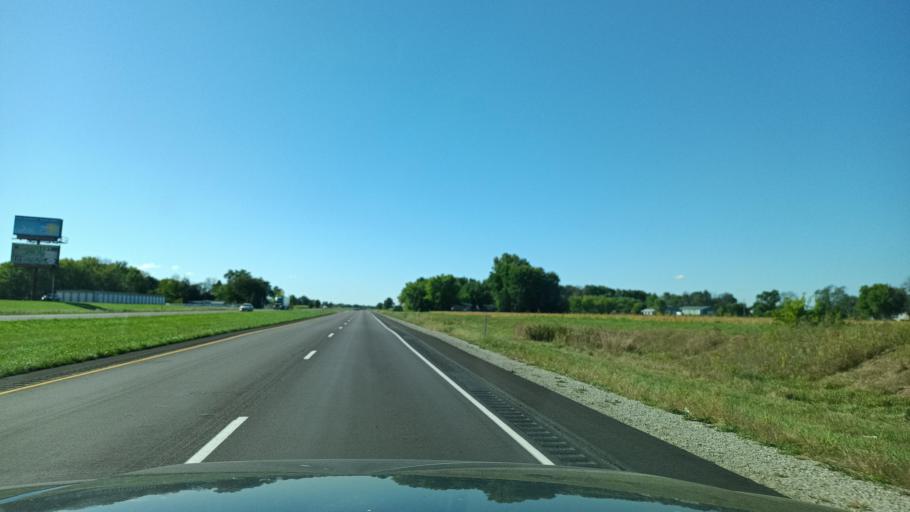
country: US
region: Illinois
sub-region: Hancock County
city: Nauvoo
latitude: 40.4751
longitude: -91.4446
